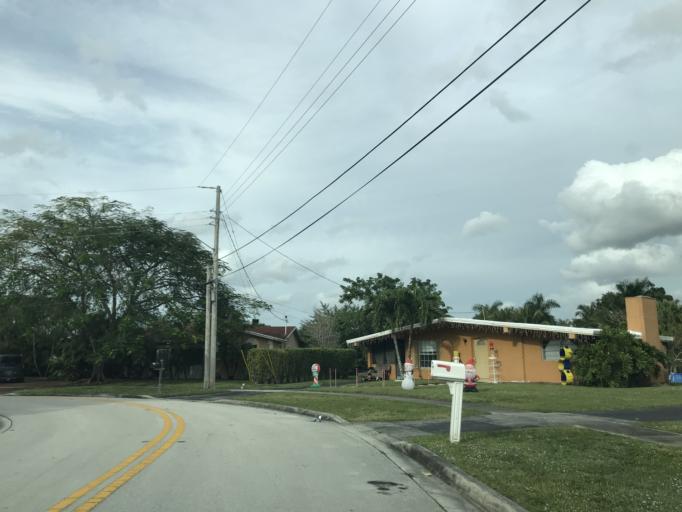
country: US
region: Florida
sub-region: Broward County
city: Margate
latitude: 26.2564
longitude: -80.2047
